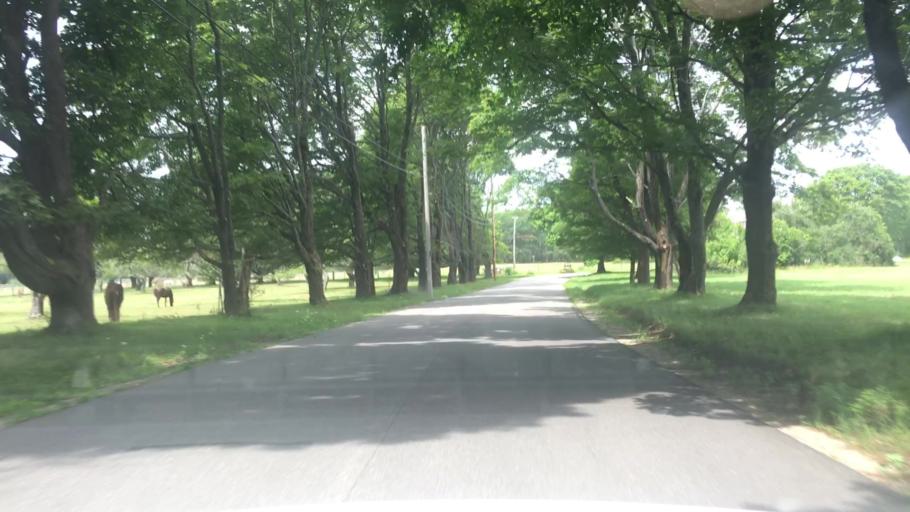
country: US
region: Maine
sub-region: Cumberland County
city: Scarborough
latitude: 43.5674
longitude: -70.2614
